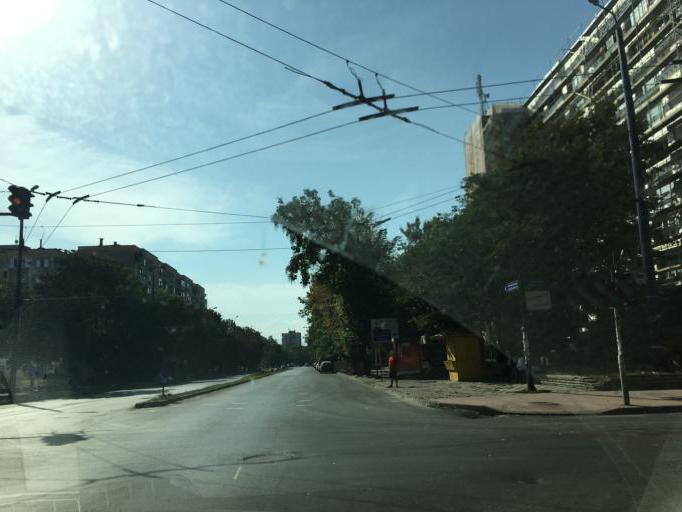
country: BG
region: Pazardzhik
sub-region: Obshtina Pazardzhik
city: Pazardzhik
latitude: 42.2052
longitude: 24.3297
